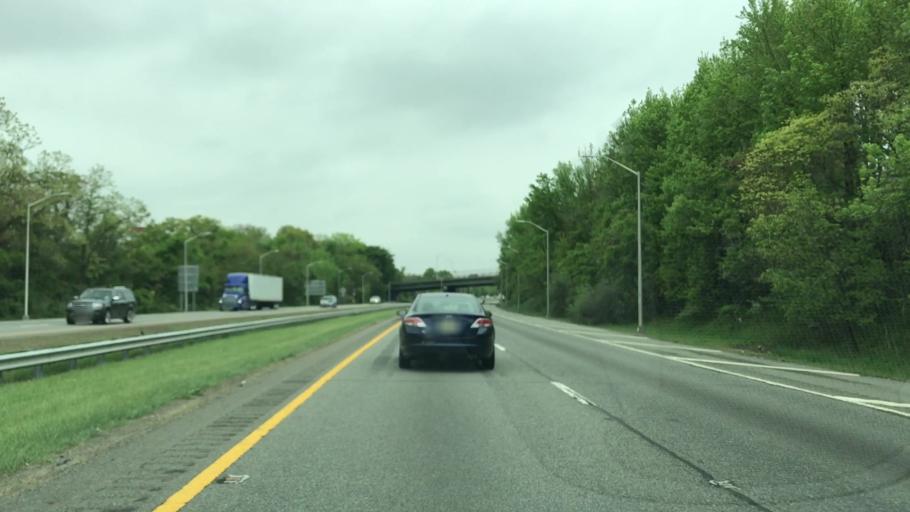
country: US
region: New Jersey
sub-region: Middlesex County
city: Carteret
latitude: 40.5459
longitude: -74.2221
